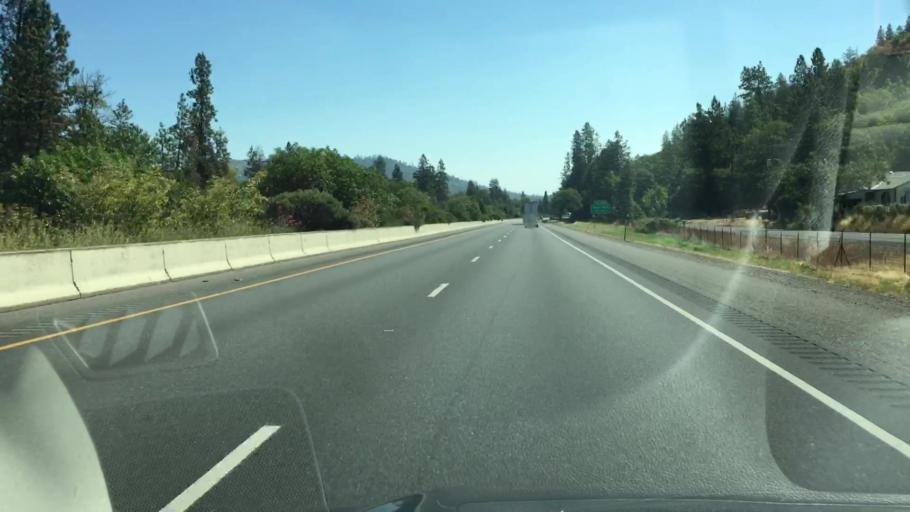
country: US
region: Oregon
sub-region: Jackson County
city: Gold Hill
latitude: 42.4296
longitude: -123.0589
